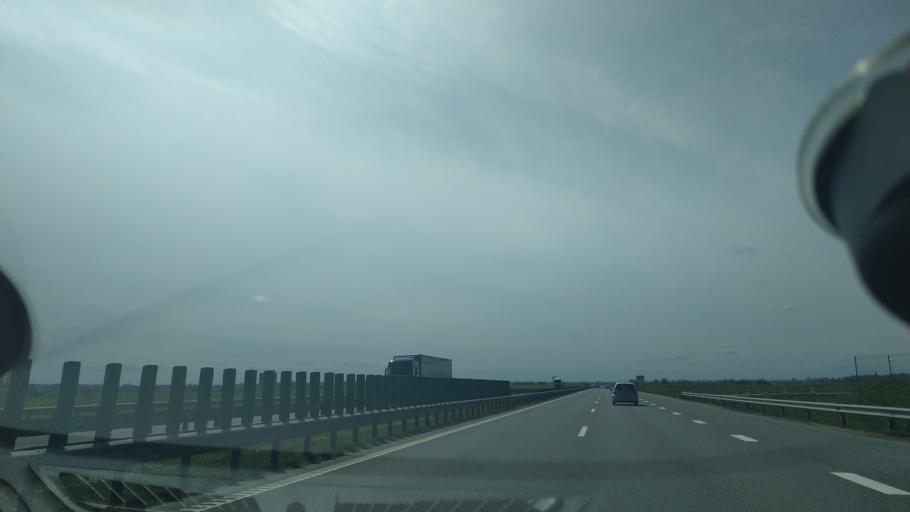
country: LT
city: Kazlu Ruda
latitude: 54.6668
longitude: 23.5158
